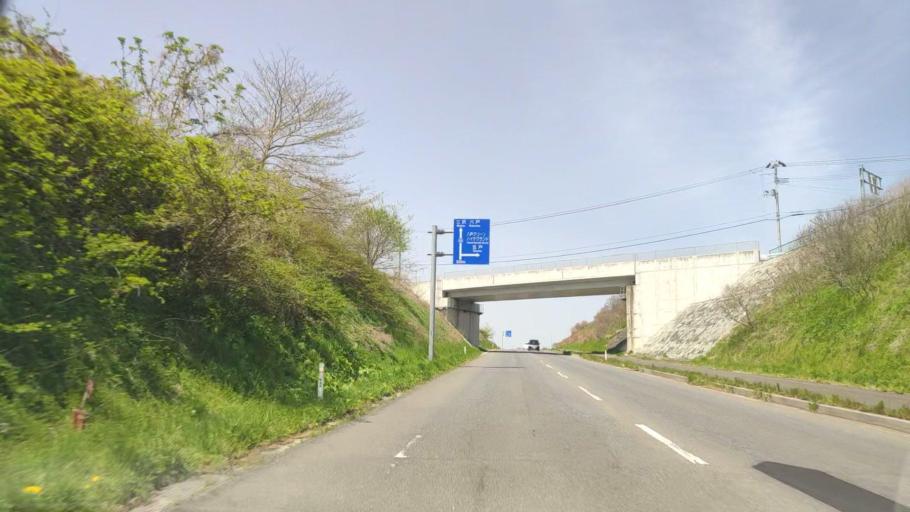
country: JP
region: Aomori
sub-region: Hachinohe Shi
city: Uchimaru
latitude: 40.5262
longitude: 141.4111
